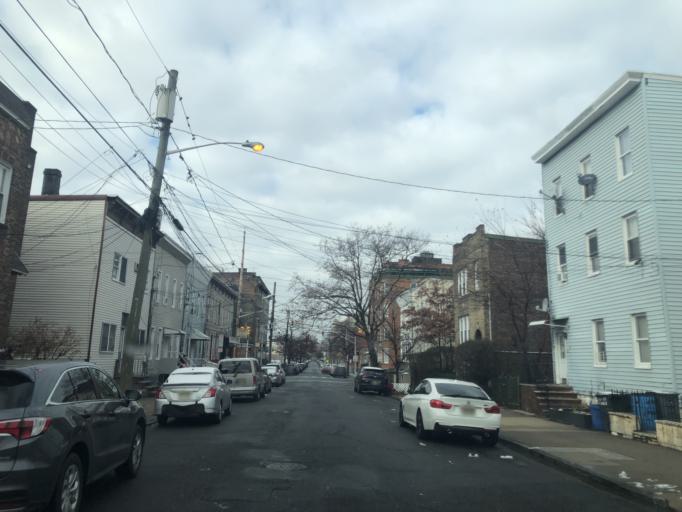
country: US
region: New Jersey
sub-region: Hudson County
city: Hoboken
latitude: 40.7344
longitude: -74.0525
